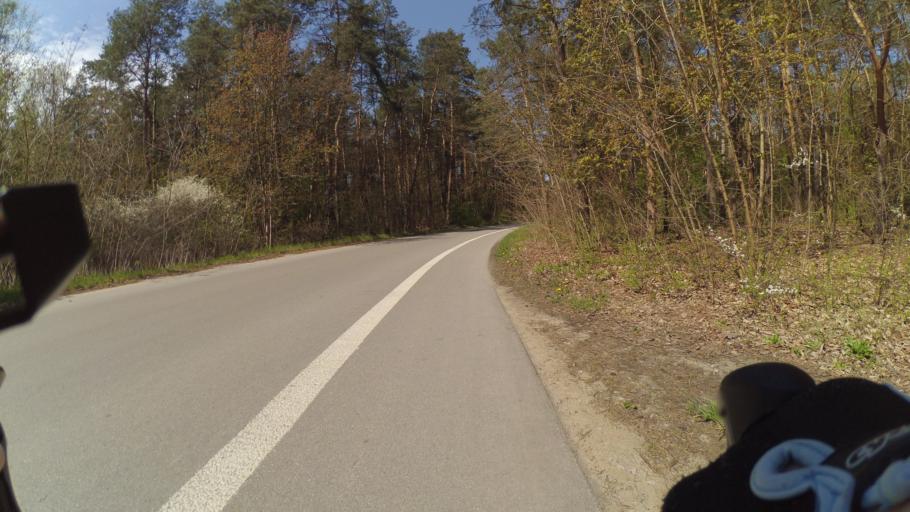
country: PL
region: Masovian Voivodeship
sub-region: Powiat nowodworski
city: Nowy Dwor Mazowiecki
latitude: 52.3928
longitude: 20.6759
